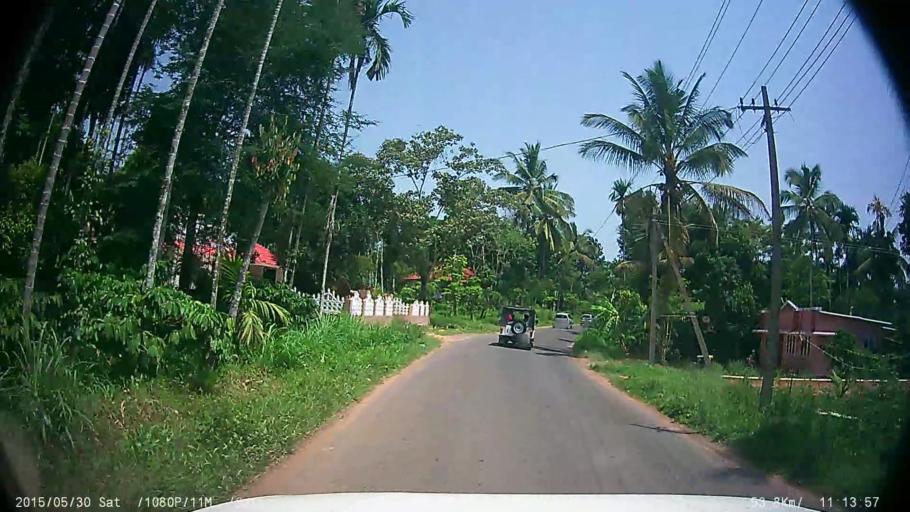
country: IN
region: Kerala
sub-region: Wayanad
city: Panamaram
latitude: 11.7640
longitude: 76.0621
